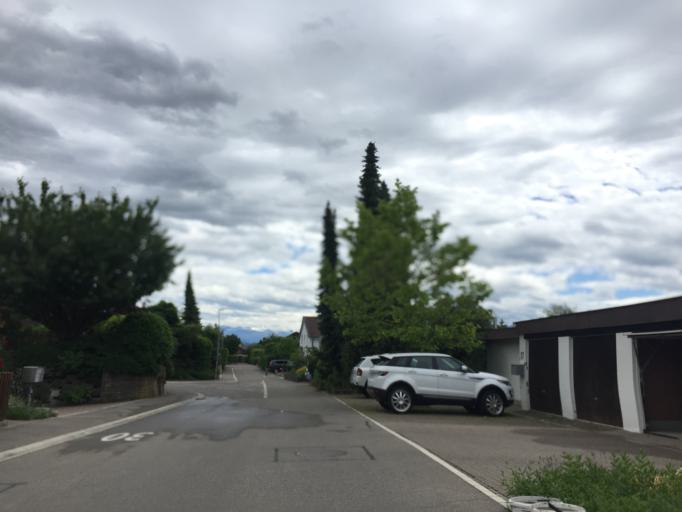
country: CH
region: Bern
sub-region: Bern-Mittelland District
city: Rubigen
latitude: 46.8955
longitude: 7.5418
